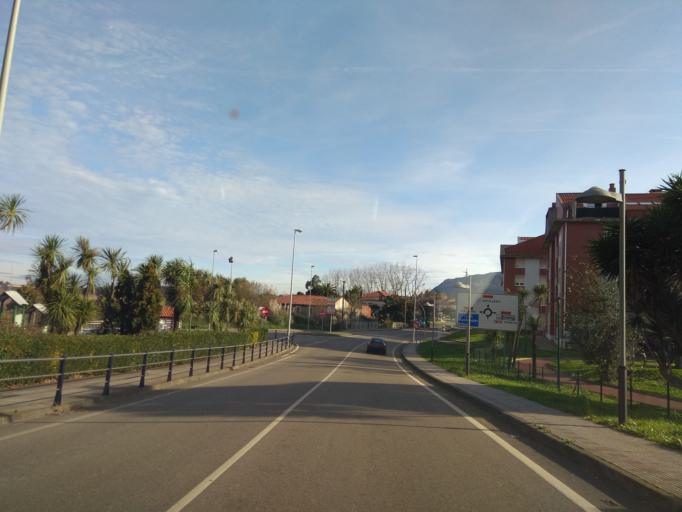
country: ES
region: Cantabria
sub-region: Provincia de Cantabria
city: El Astillero
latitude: 43.4058
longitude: -3.8394
